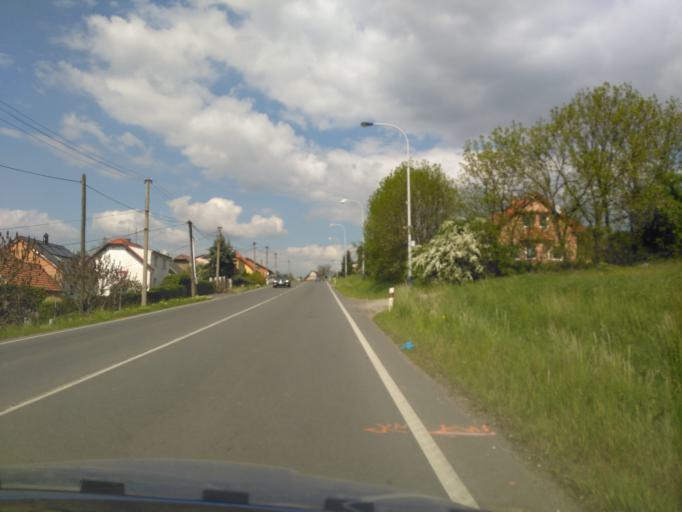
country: CZ
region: Central Bohemia
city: Zdice
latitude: 49.9303
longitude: 14.0050
